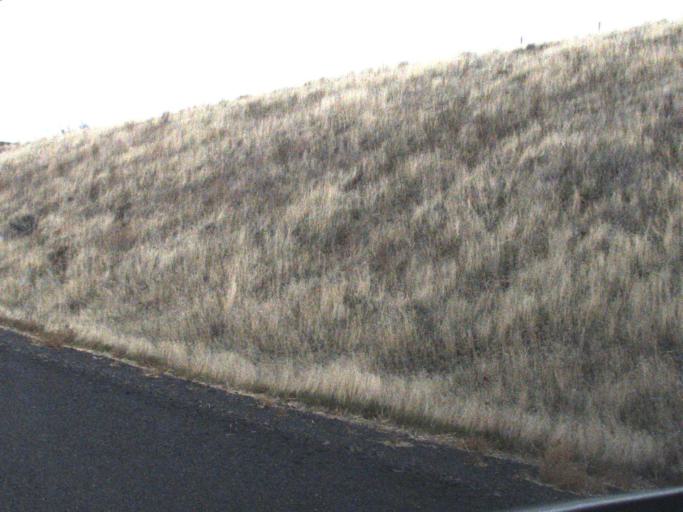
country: US
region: Washington
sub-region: Columbia County
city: Dayton
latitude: 46.7716
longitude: -118.0377
